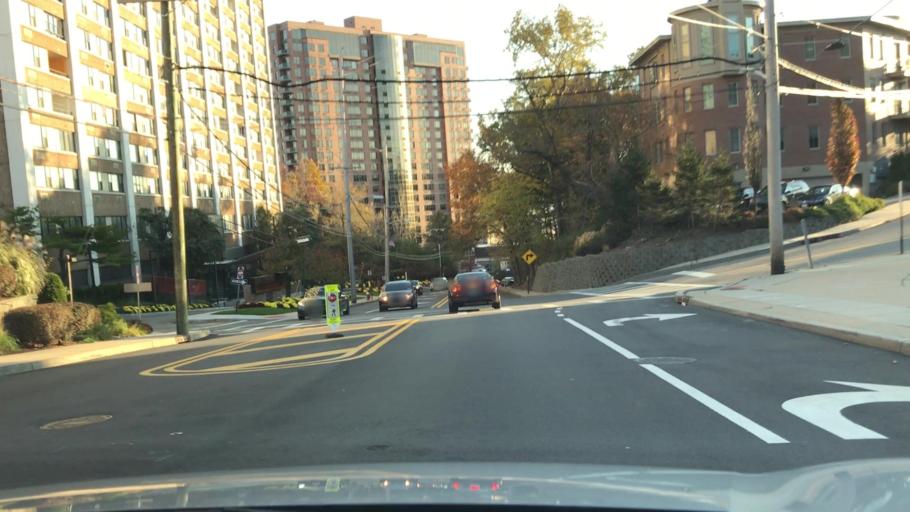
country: US
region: New Jersey
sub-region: Bergen County
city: Cliffside Park
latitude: 40.8133
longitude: -73.9903
